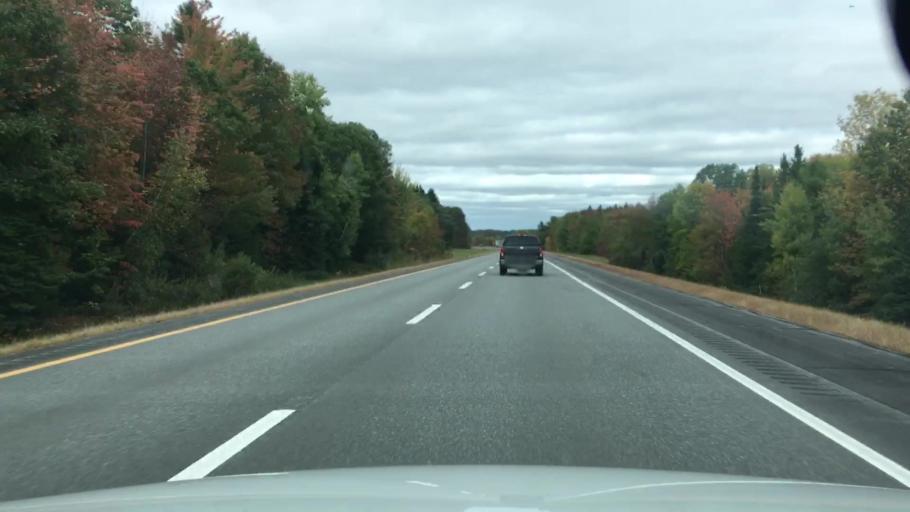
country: US
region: Maine
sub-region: Somerset County
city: Pittsfield
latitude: 44.7633
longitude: -69.4136
